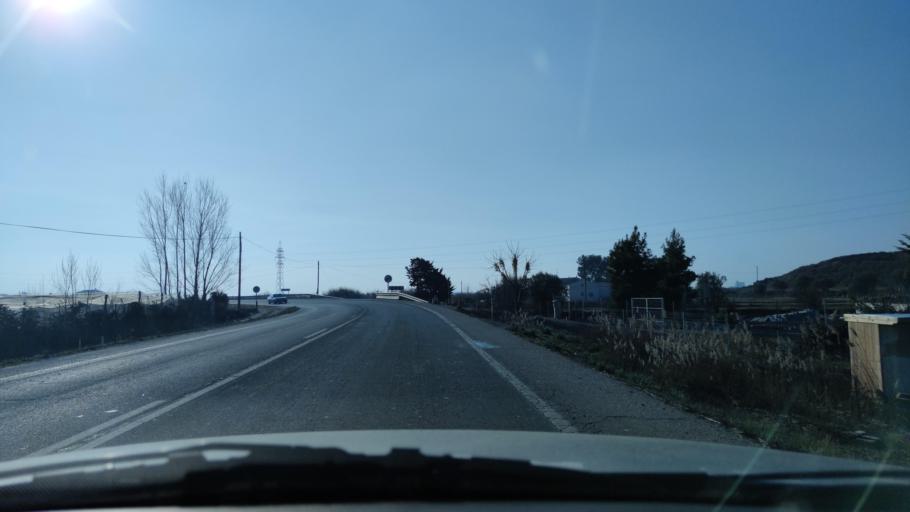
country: ES
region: Catalonia
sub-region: Provincia de Lleida
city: Torrefarrera
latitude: 41.6586
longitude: 0.6310
